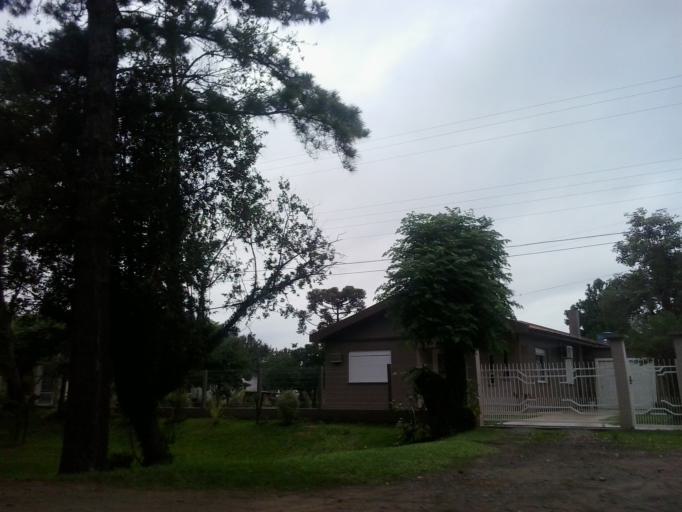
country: BR
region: Rio Grande do Sul
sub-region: Santa Maria
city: Santa Maria
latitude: -29.7224
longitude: -53.3842
